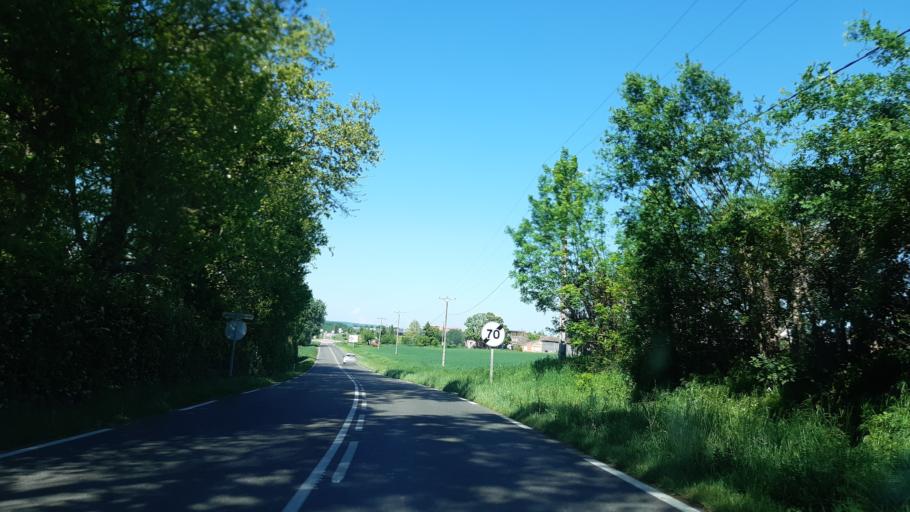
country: FR
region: Midi-Pyrenees
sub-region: Departement du Gers
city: Pujaudran
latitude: 43.5973
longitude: 1.0648
